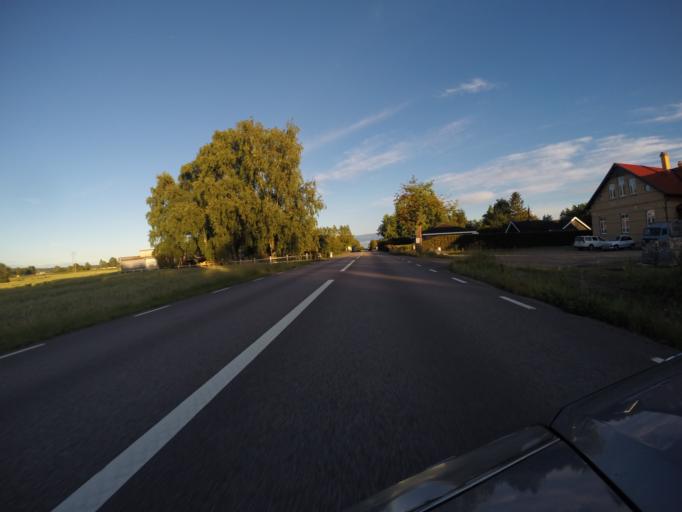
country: SE
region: Skane
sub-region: Helsingborg
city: Hyllinge
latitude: 56.1210
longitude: 12.8861
